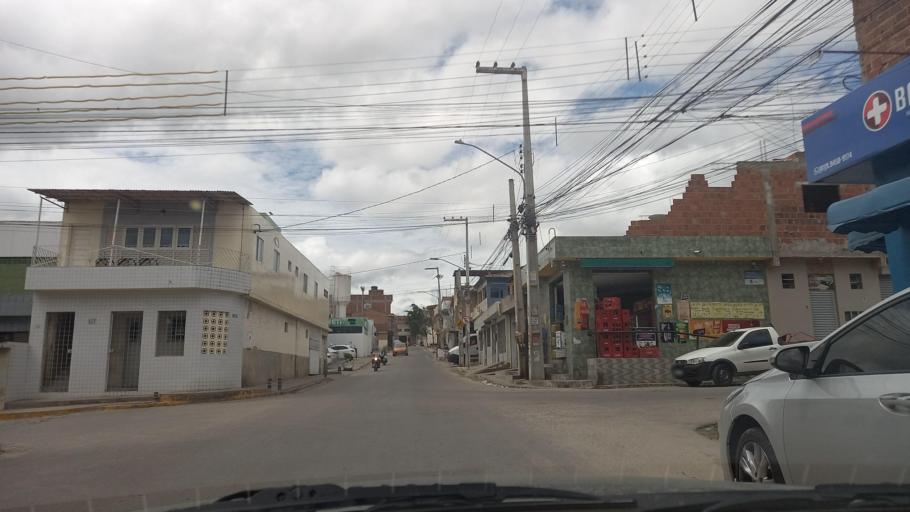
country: BR
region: Pernambuco
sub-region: Caruaru
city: Caruaru
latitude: -8.2722
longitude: -35.9559
